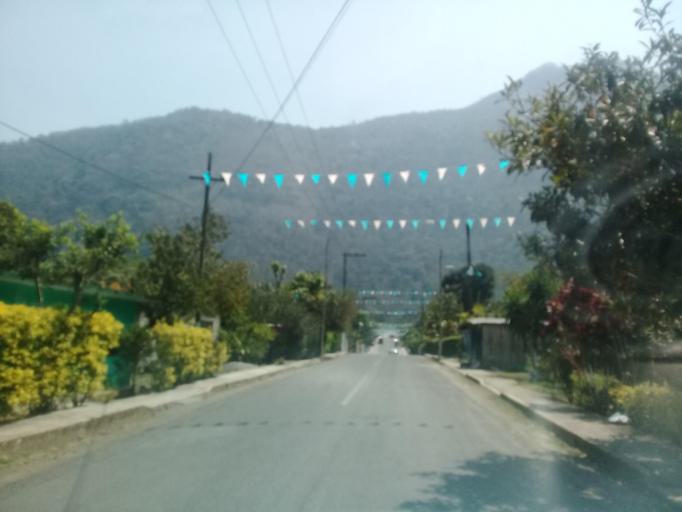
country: MX
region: Veracruz
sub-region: Ixtaczoquitlan
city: Capoluca
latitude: 18.8050
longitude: -96.9899
